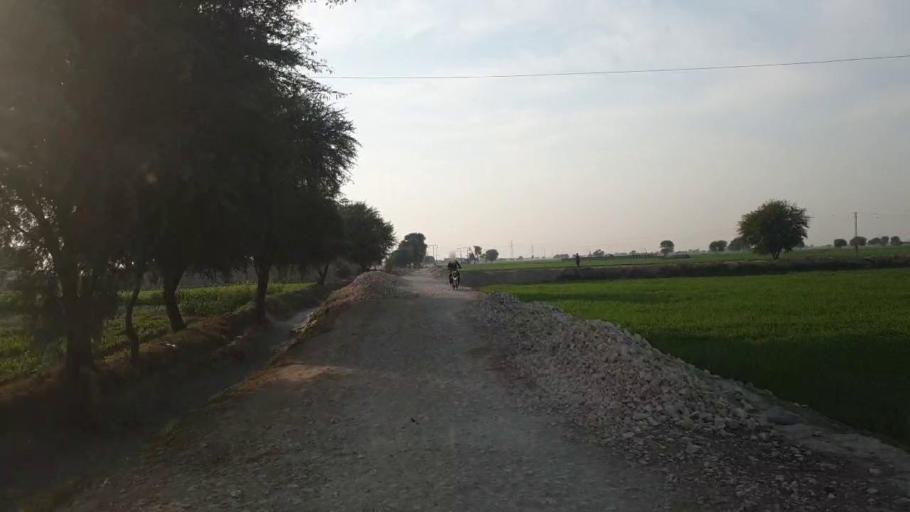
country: PK
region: Sindh
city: Shahpur Chakar
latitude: 26.1523
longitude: 68.6287
